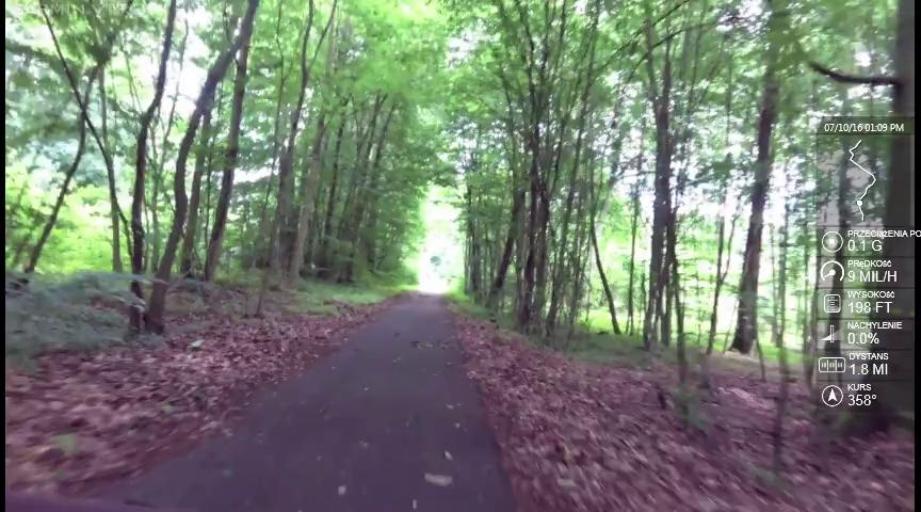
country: PL
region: West Pomeranian Voivodeship
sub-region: Powiat gryfinski
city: Banie
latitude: 53.0628
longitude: 14.6273
